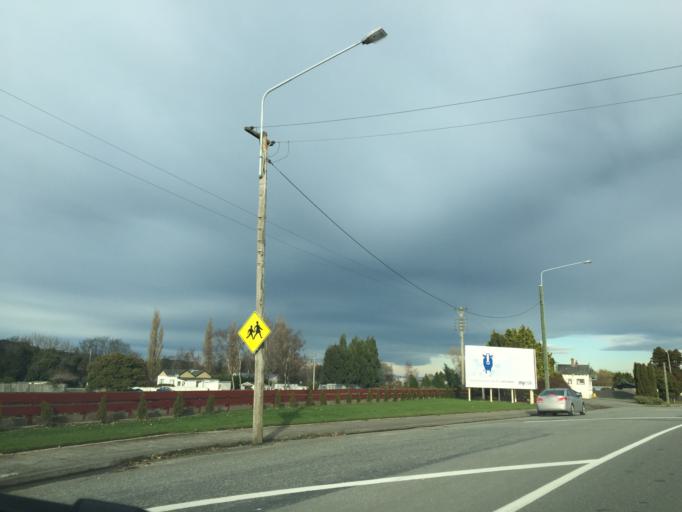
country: NZ
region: Southland
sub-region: Gore District
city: Gore
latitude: -46.1947
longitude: 168.8645
